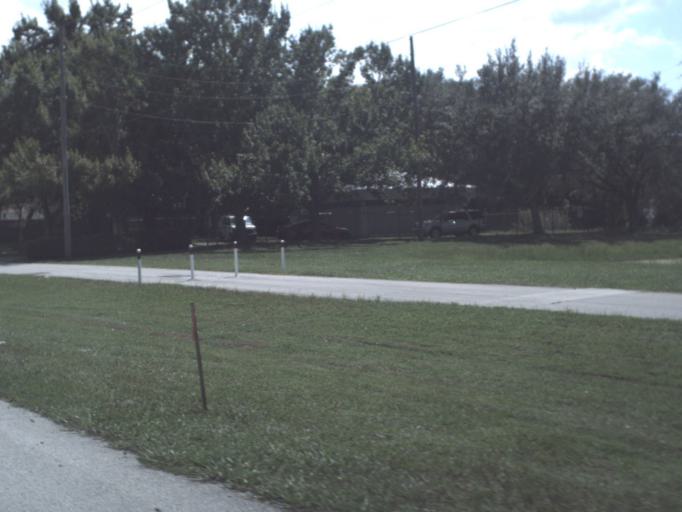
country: US
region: Florida
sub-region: Pinellas County
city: East Lake
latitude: 28.1230
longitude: -82.6962
